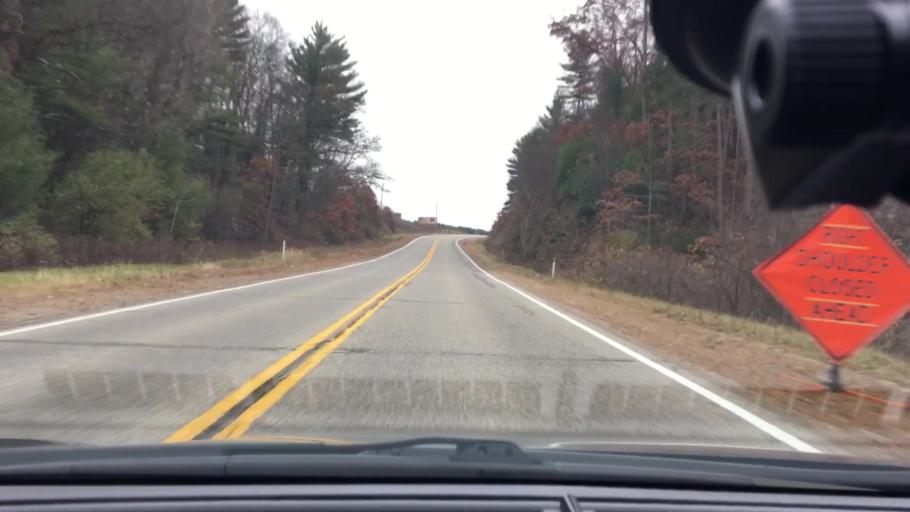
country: US
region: Wisconsin
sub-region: Columbia County
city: Wisconsin Dells
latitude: 43.6400
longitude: -89.8001
